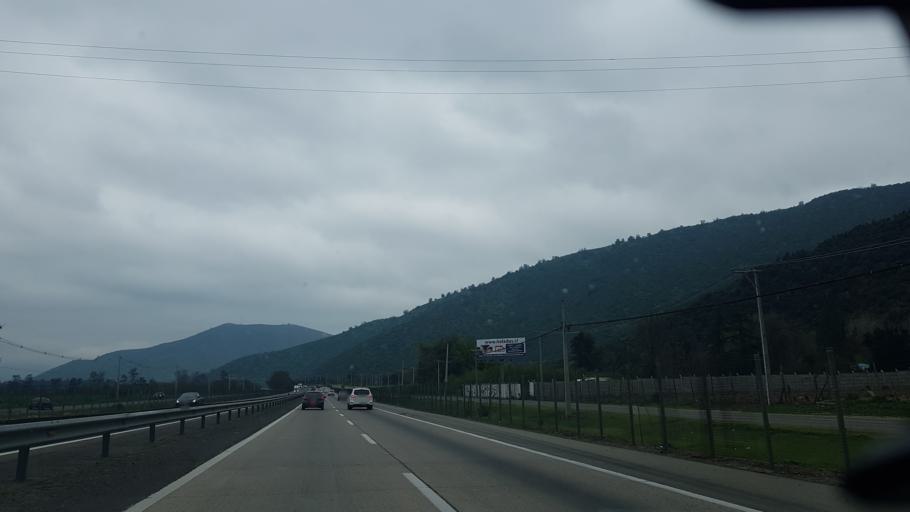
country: CL
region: Santiago Metropolitan
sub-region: Provincia de Chacabuco
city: Lampa
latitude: -33.4026
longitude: -71.0971
